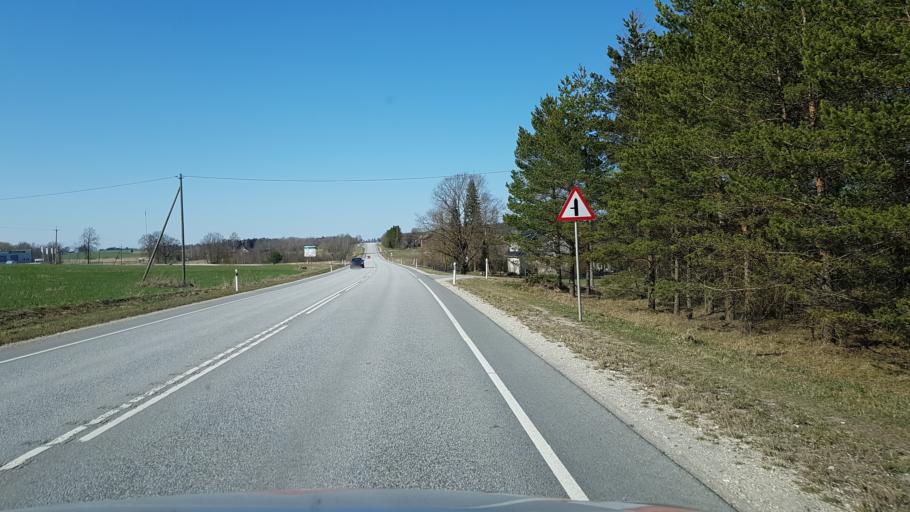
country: EE
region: Tartu
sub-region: Tartu linn
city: Tartu
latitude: 58.4909
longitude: 26.7770
